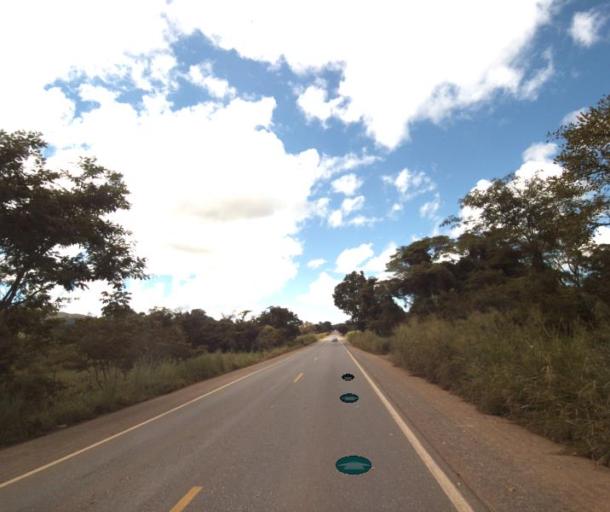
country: BR
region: Goias
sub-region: Petrolina De Goias
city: Petrolina de Goias
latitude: -15.9677
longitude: -49.1734
